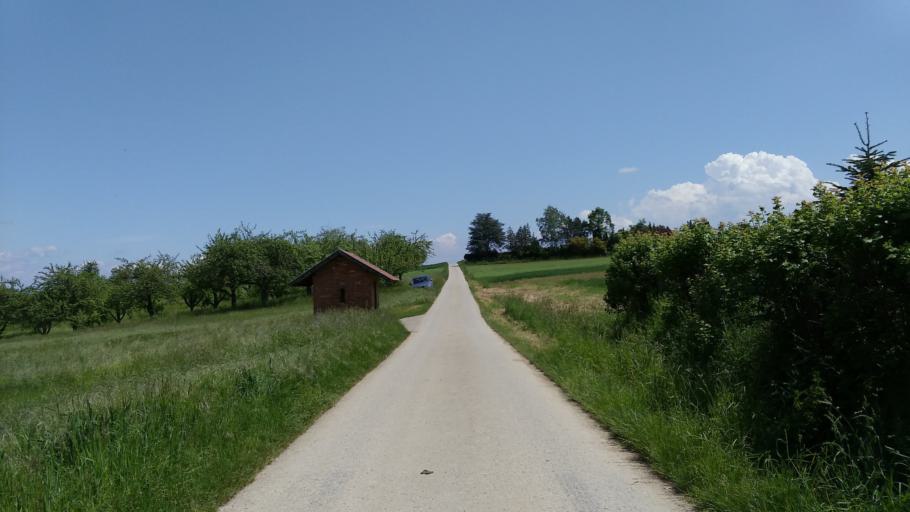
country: DE
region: Baden-Wuerttemberg
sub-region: Regierungsbezirk Stuttgart
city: Nurtingen
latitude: 48.6327
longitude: 9.3584
